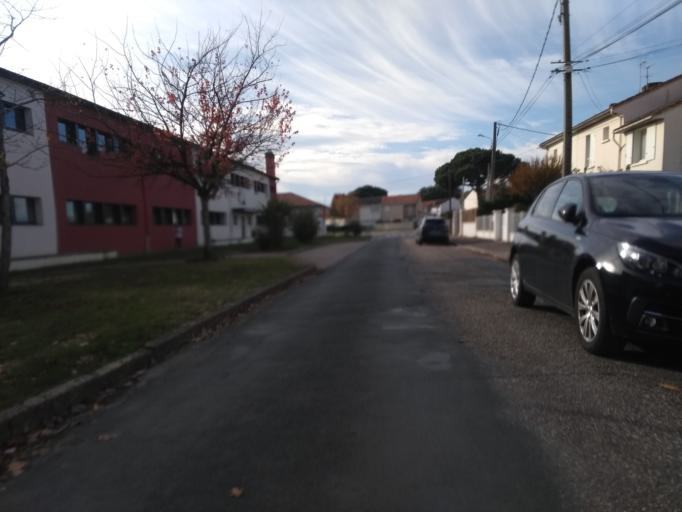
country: FR
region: Aquitaine
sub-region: Departement de la Gironde
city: Pessac
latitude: 44.8001
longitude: -0.6760
